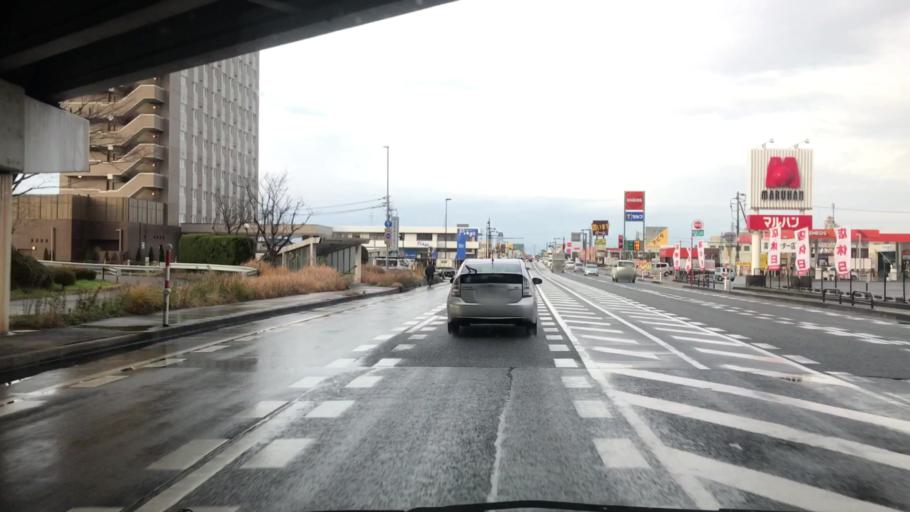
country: JP
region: Toyama
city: Toyama-shi
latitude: 36.6543
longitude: 137.2097
